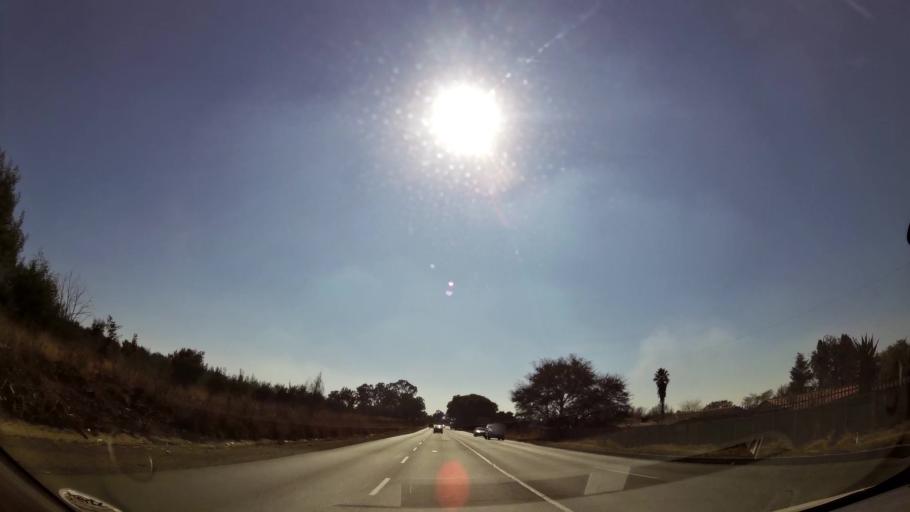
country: ZA
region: Mpumalanga
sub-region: Nkangala District Municipality
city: Witbank
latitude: -25.8474
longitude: 29.2360
